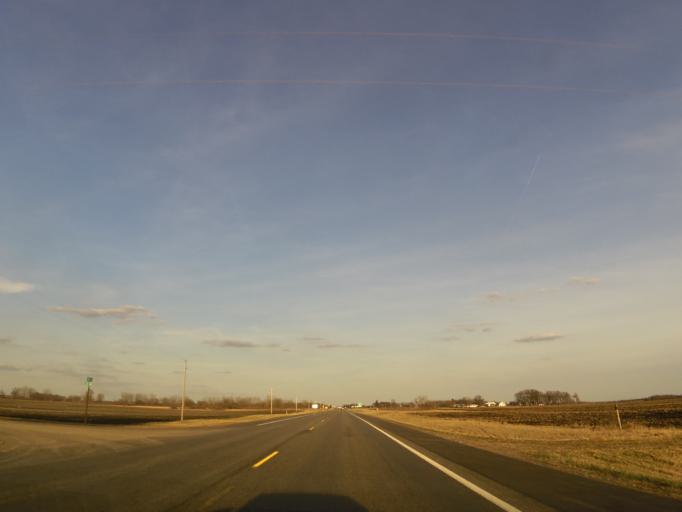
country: US
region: Minnesota
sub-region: McLeod County
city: Glencoe
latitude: 44.7396
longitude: -94.2240
